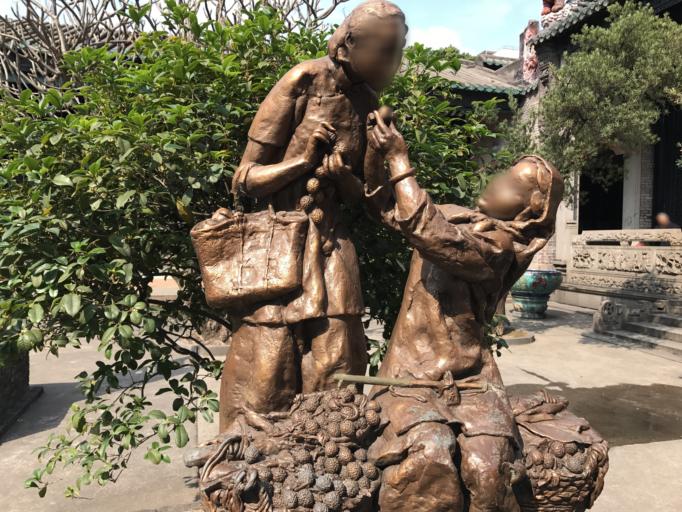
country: CN
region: Guangdong
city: Guangzhou
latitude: 23.1297
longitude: 113.2400
